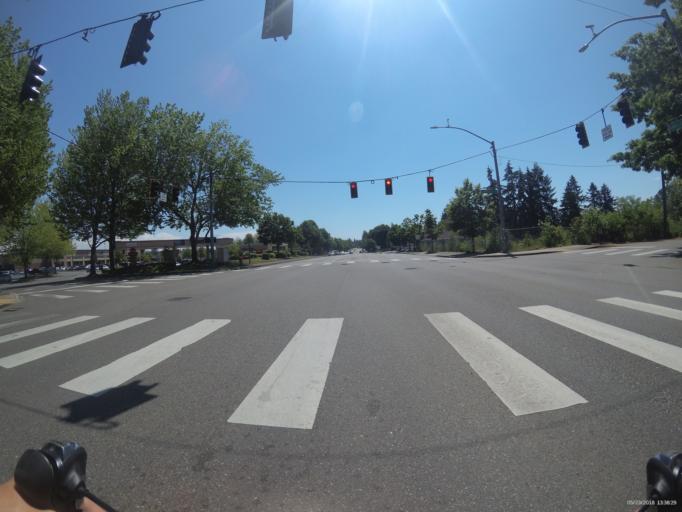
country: US
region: Washington
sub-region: Pierce County
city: Lakewood
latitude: 47.1657
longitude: -122.5207
